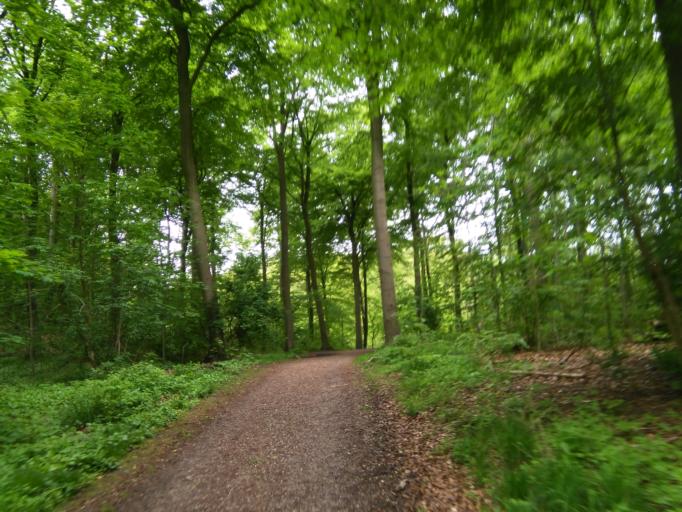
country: DK
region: Central Jutland
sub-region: Arhus Kommune
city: Arhus
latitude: 56.1212
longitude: 10.2040
